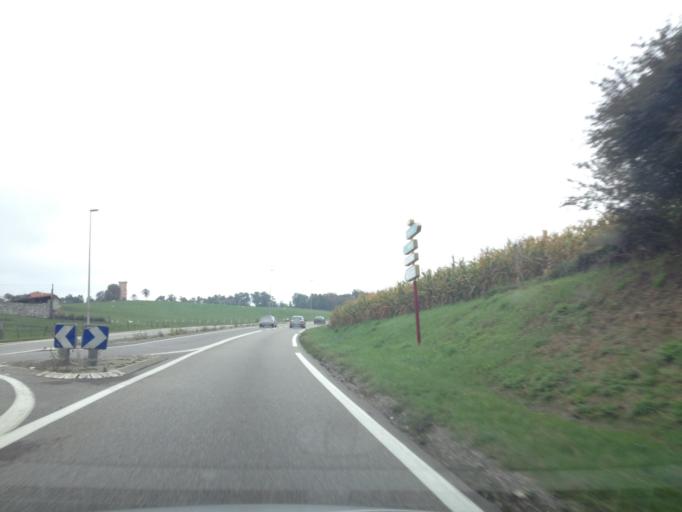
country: FR
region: Rhone-Alpes
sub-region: Departement de la Haute-Savoie
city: Seynod
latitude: 45.8707
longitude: 6.0746
